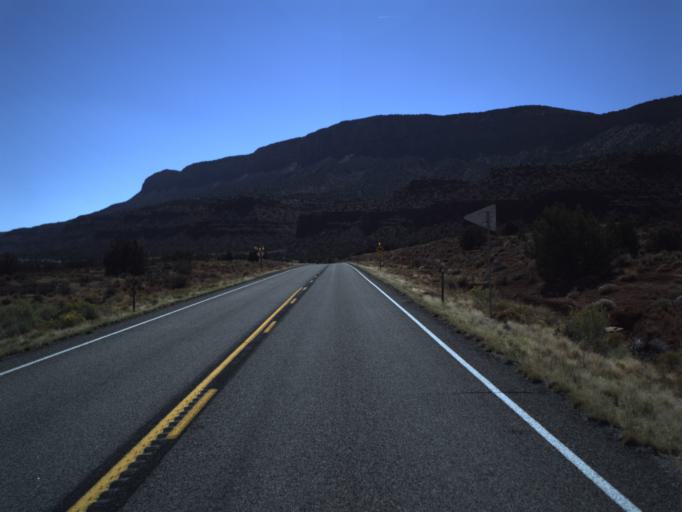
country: US
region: Utah
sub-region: San Juan County
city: Blanding
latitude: 37.6875
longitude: -110.2231
